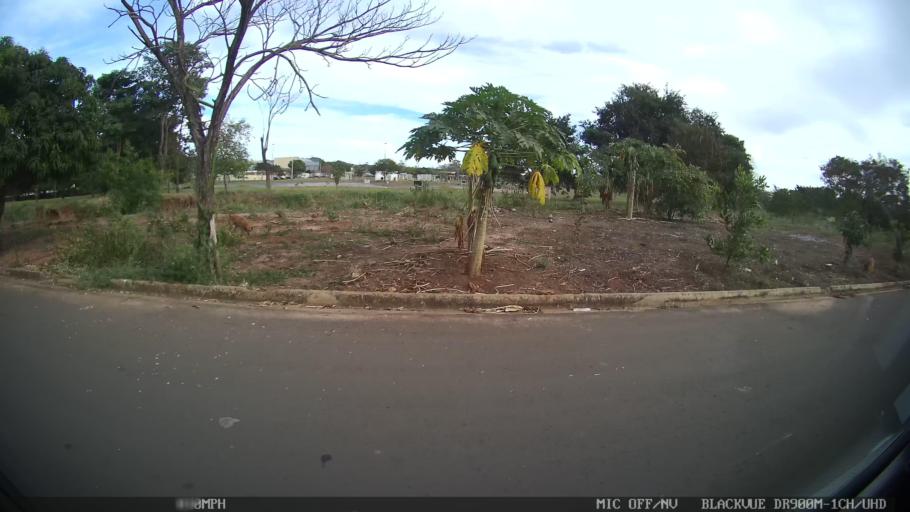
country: BR
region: Sao Paulo
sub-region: Catanduva
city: Catanduva
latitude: -21.1236
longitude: -48.9829
